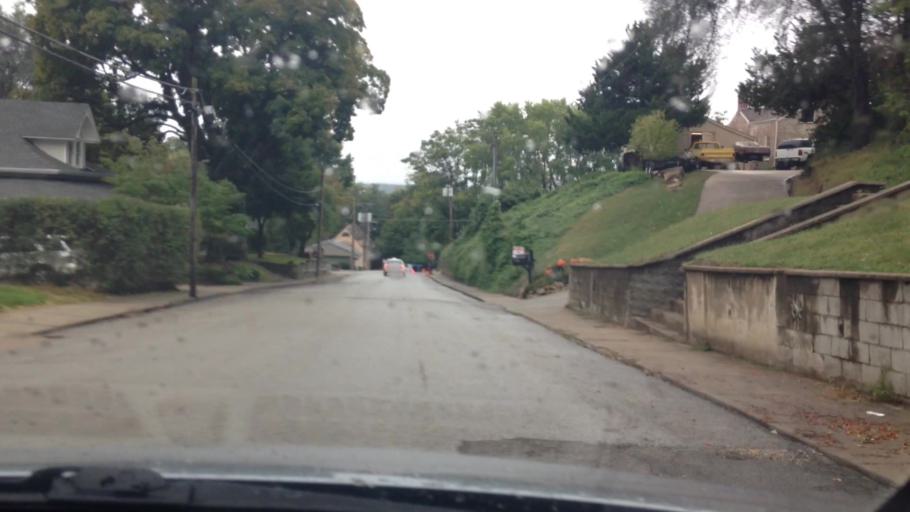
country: US
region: Missouri
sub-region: Platte County
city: Weston
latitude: 39.4126
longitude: -94.8990
